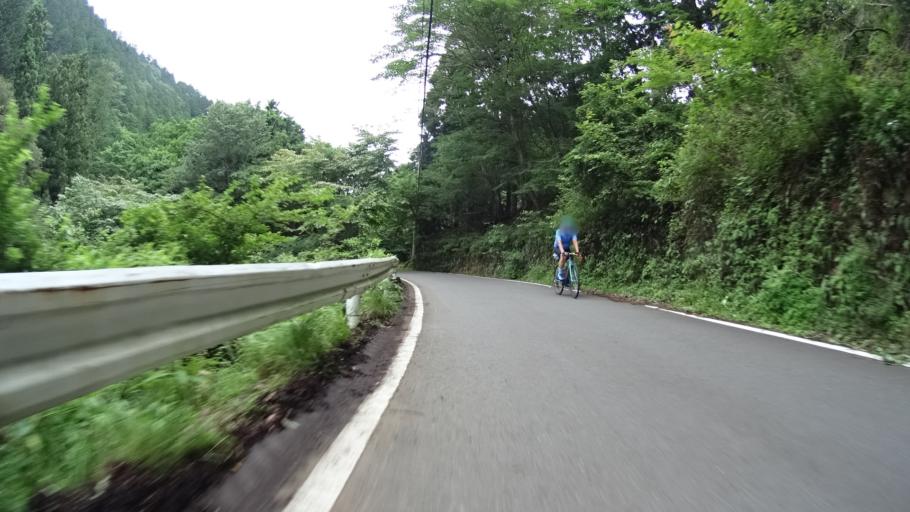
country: JP
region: Kanagawa
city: Hadano
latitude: 35.4382
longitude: 139.2108
